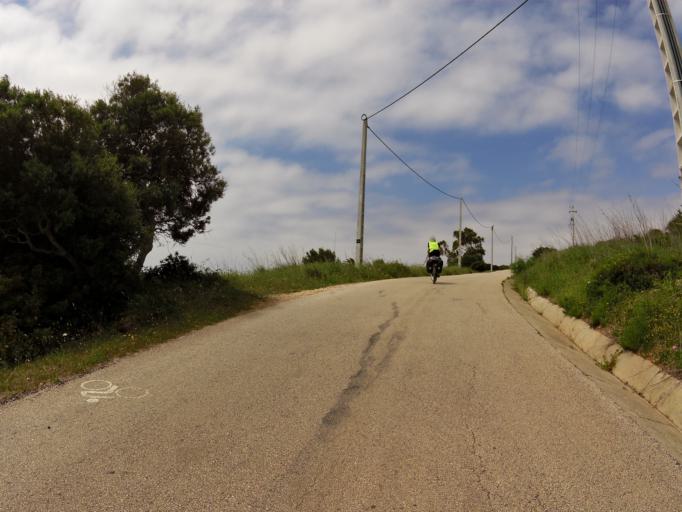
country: PT
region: Faro
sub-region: Vila do Bispo
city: Vila do Bispo
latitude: 37.0669
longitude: -8.8620
